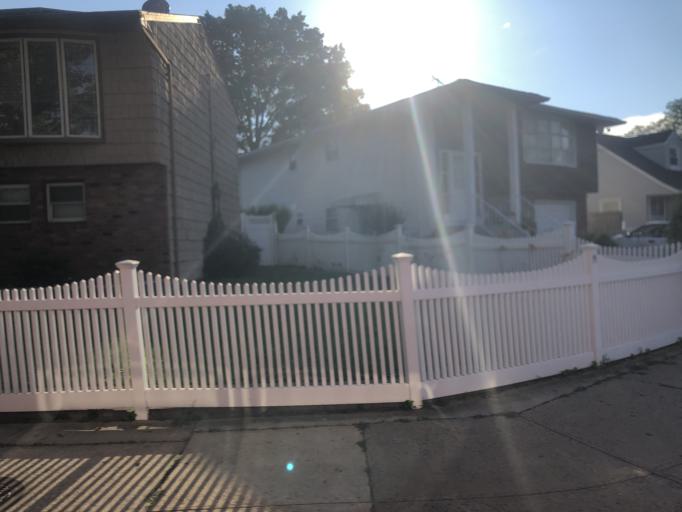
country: US
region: New York
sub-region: Nassau County
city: Malverne
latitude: 40.6783
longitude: -73.6840
